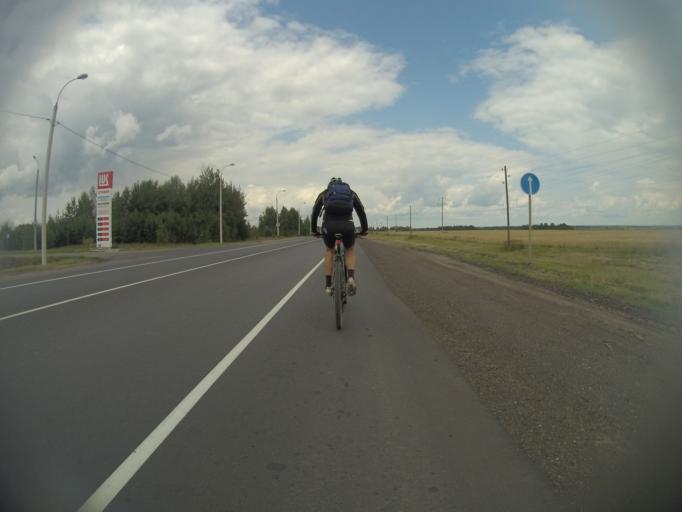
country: RU
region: Vladimir
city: Suzdal'
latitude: 56.4444
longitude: 40.4652
